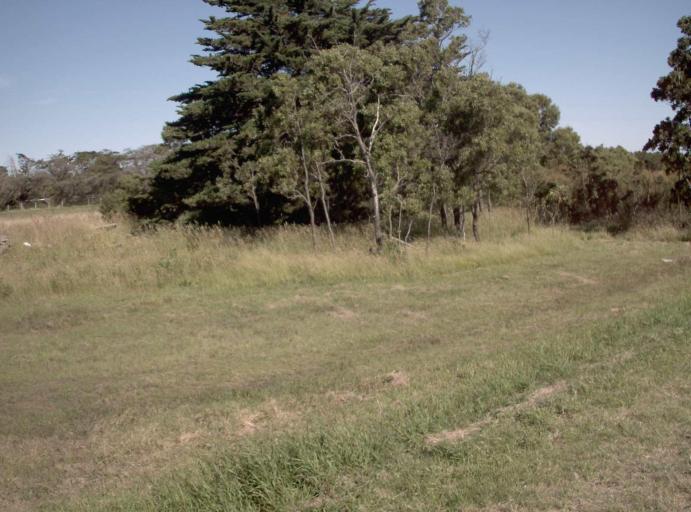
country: AU
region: Victoria
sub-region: Latrobe
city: Traralgon
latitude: -38.6282
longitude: 146.6764
